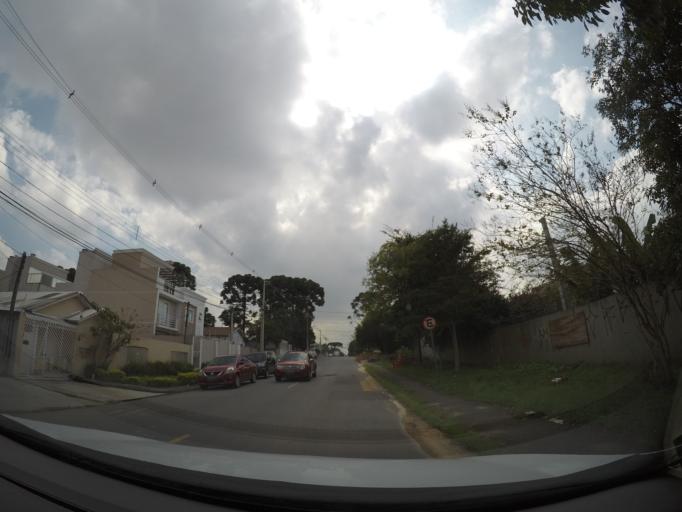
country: BR
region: Parana
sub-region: Sao Jose Dos Pinhais
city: Sao Jose dos Pinhais
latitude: -25.5014
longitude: -49.2402
